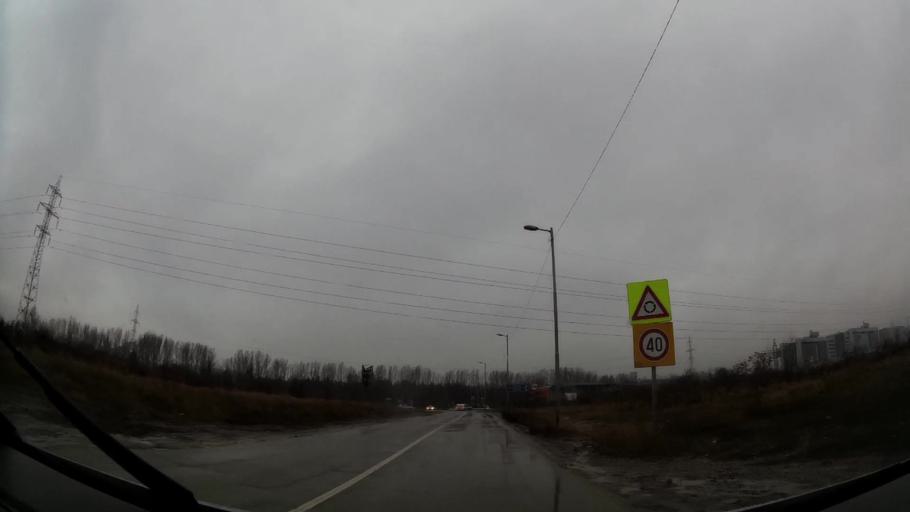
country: BG
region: Sofia-Capital
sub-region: Stolichna Obshtina
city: Sofia
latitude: 42.6242
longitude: 23.3854
